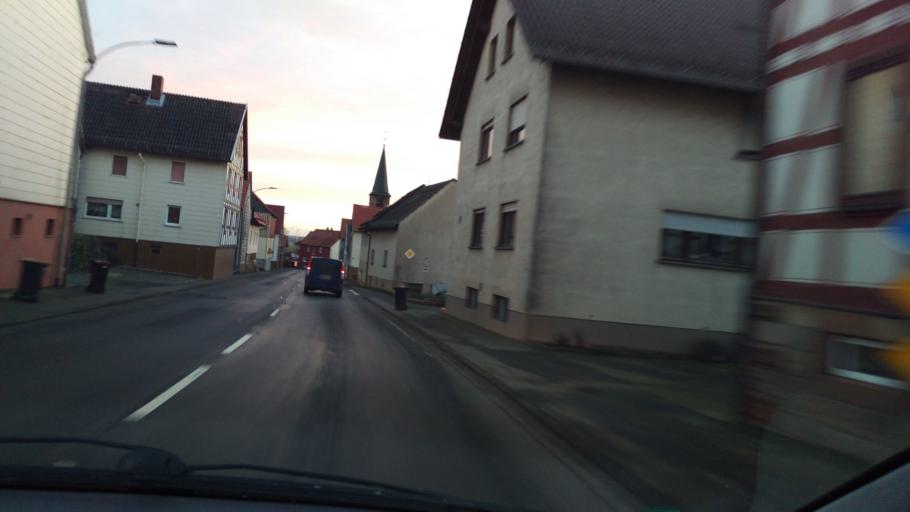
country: DE
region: Hesse
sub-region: Regierungsbezirk Giessen
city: Homberg
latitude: 50.7456
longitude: 9.0432
